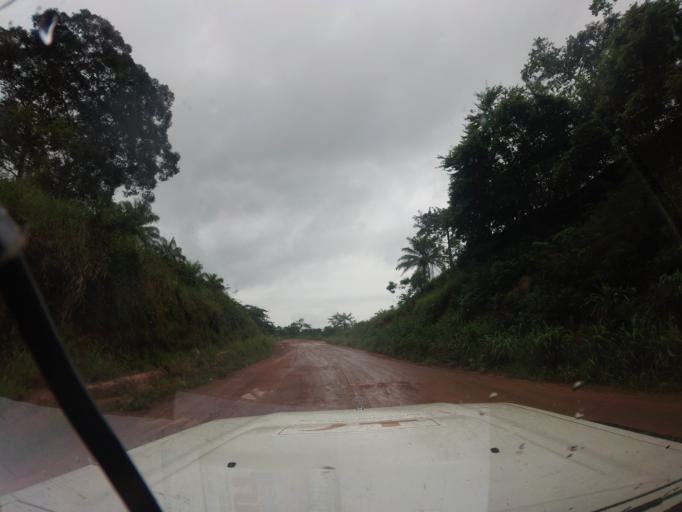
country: SL
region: Eastern Province
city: Tefeya
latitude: 8.5694
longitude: -11.2863
